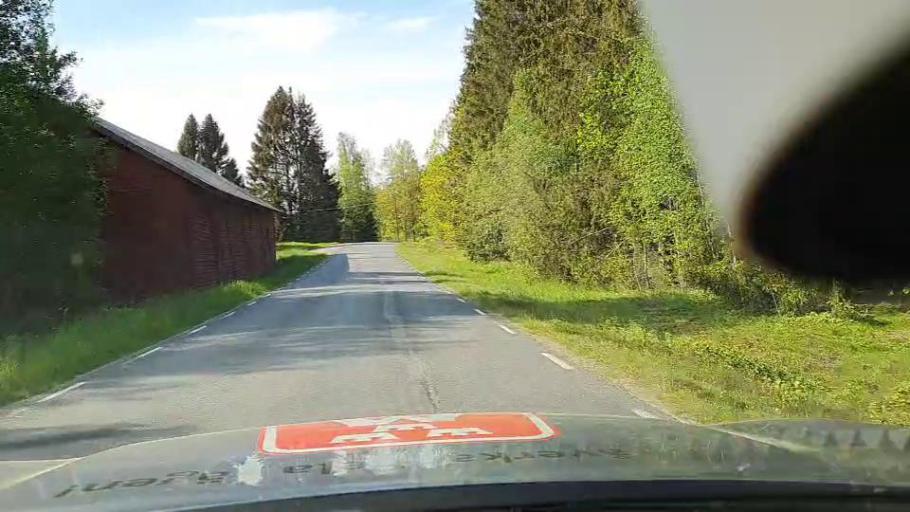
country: SE
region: Soedermanland
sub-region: Eskilstuna Kommun
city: Arla
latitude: 59.2617
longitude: 16.6546
